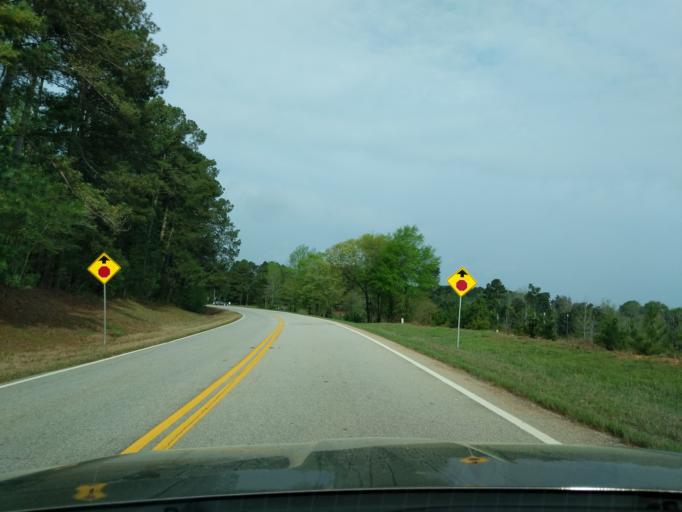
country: US
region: Georgia
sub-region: Lincoln County
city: Lincolnton
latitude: 33.8054
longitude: -82.3942
